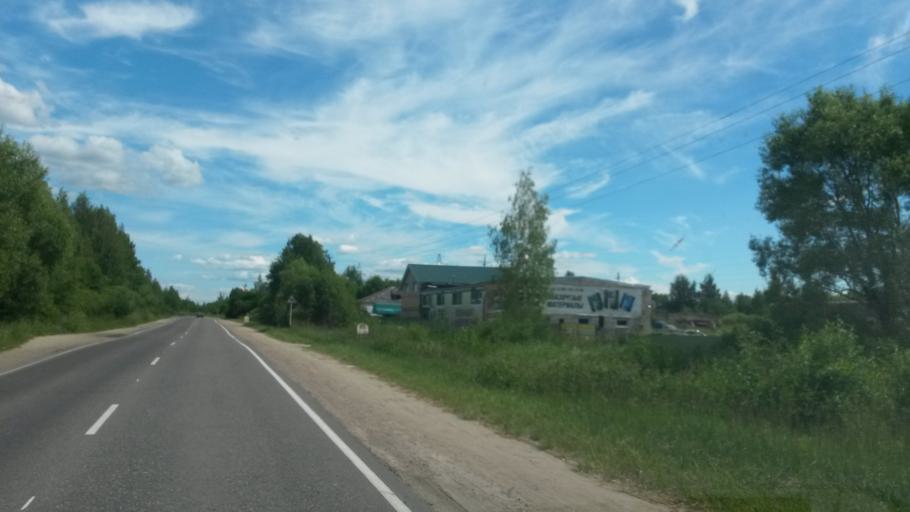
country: RU
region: Ivanovo
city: Zavolzhsk
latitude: 57.5044
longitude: 42.1045
